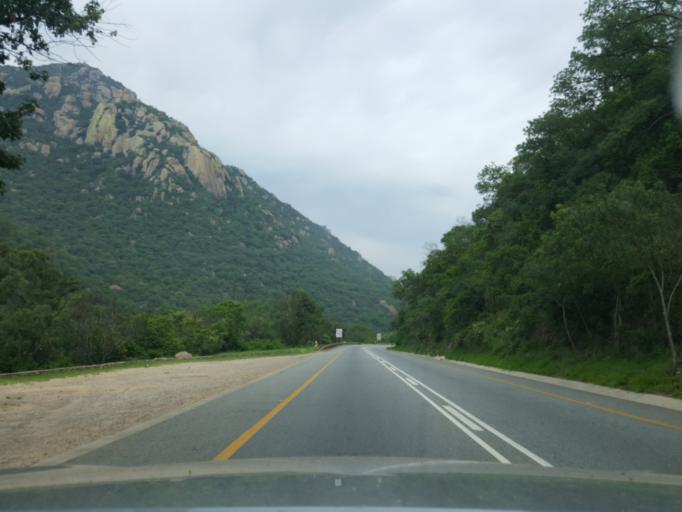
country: ZA
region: Mpumalanga
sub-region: Ehlanzeni District
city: Nelspruit
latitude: -25.5185
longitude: 31.2371
